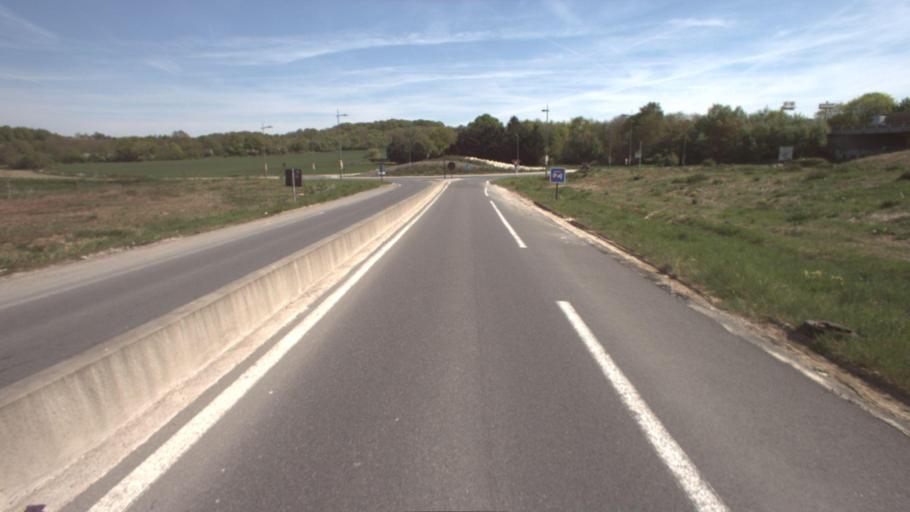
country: FR
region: Ile-de-France
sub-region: Departement de Seine-et-Marne
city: Dammartin-en-Goele
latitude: 49.0405
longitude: 2.6822
